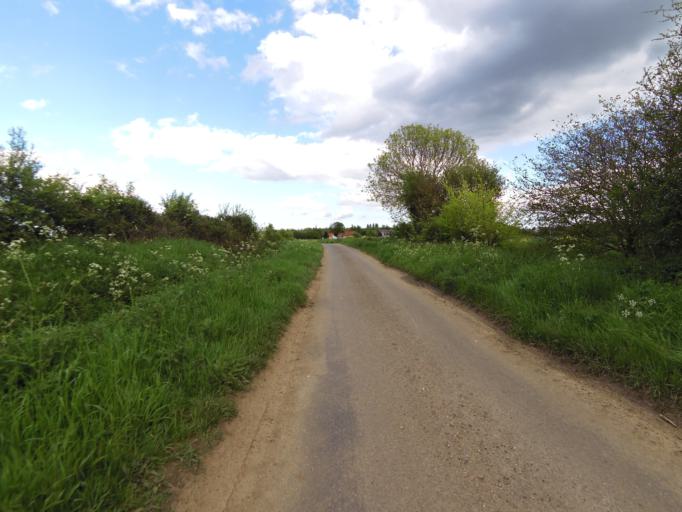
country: GB
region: England
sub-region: Suffolk
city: Elmswell
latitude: 52.2052
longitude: 0.9424
